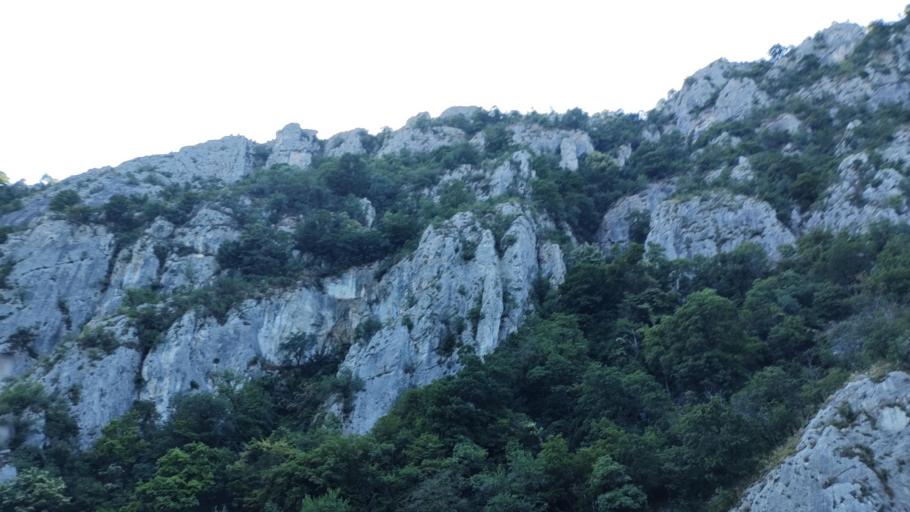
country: RO
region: Mehedinti
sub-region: Comuna Dubova
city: Dubova
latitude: 44.5921
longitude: 22.2603
